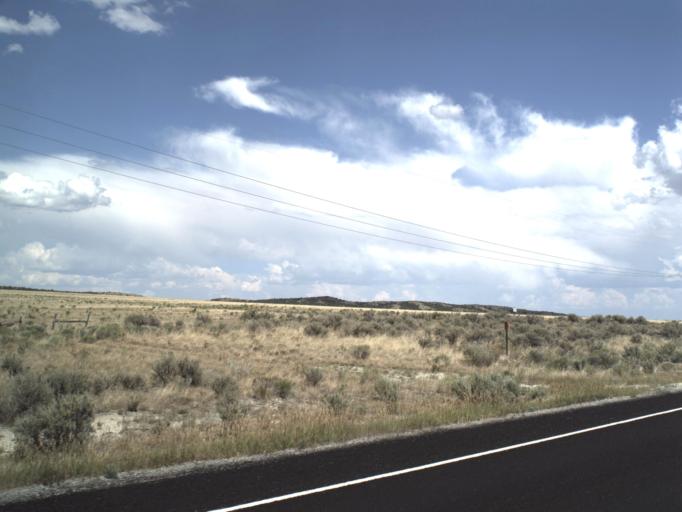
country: US
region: Idaho
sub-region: Minidoka County
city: Rupert
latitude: 41.9956
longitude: -113.1908
